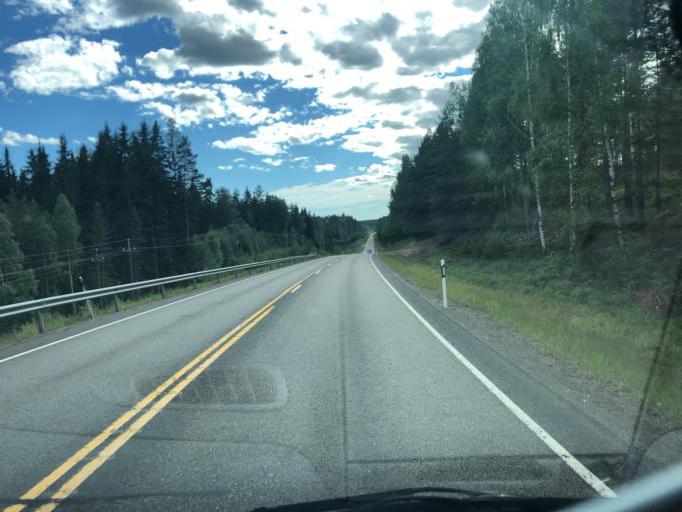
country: FI
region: Kymenlaakso
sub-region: Kouvola
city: Kouvola
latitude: 60.9735
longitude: 26.9012
